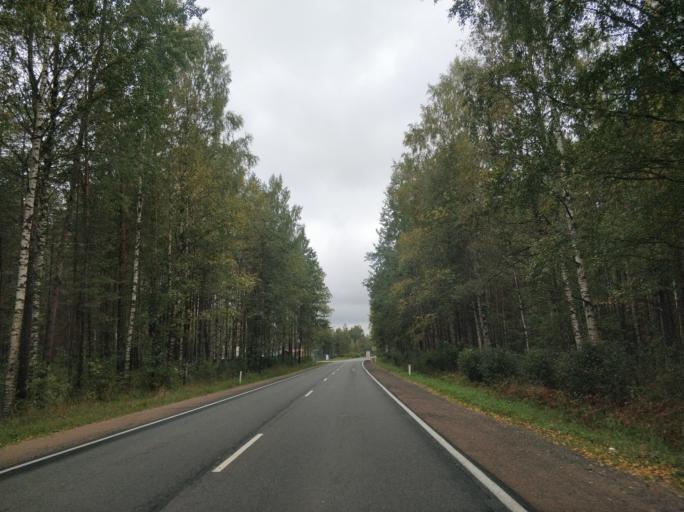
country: RU
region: Leningrad
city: Borisova Griva
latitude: 60.0912
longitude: 30.8576
